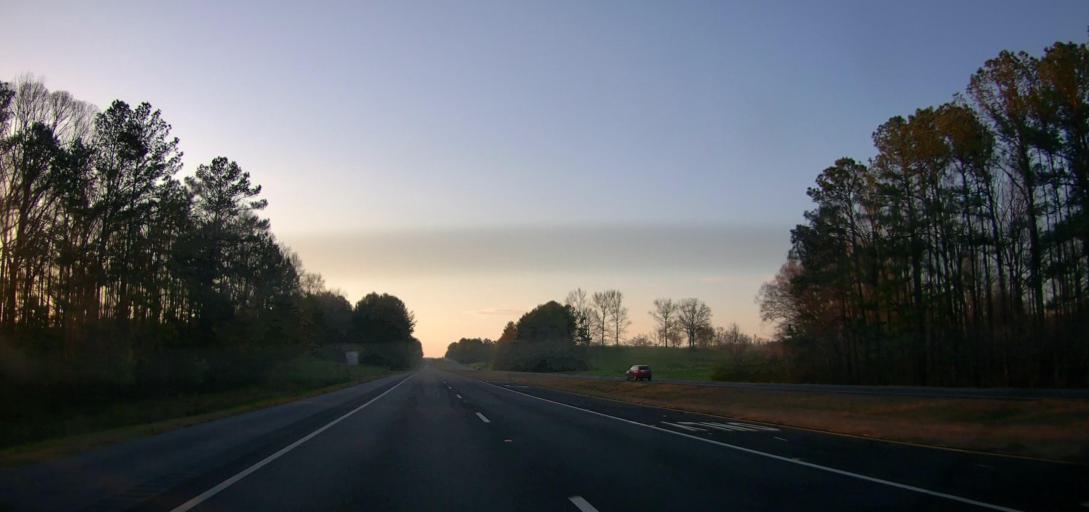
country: US
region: Alabama
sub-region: Coosa County
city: Stewartville
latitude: 33.0993
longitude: -86.2214
